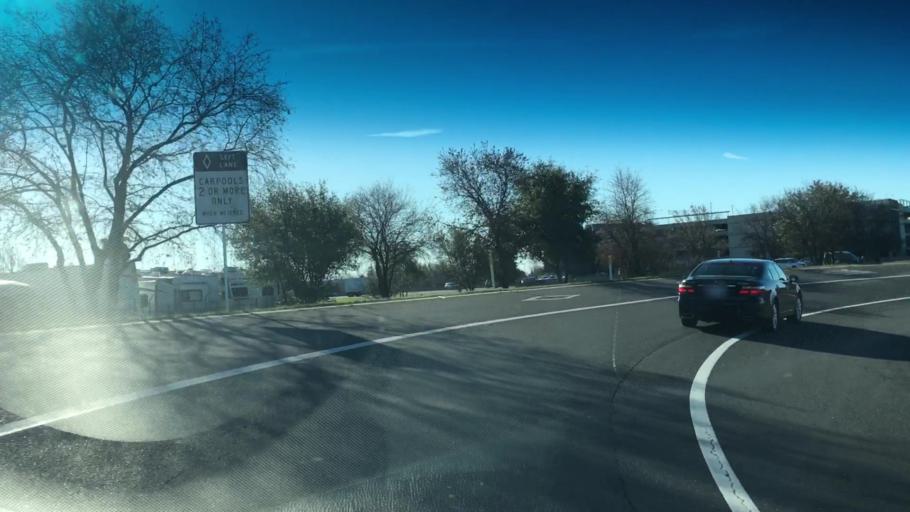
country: US
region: California
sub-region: Sacramento County
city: Florin
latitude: 38.4737
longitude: -121.4207
